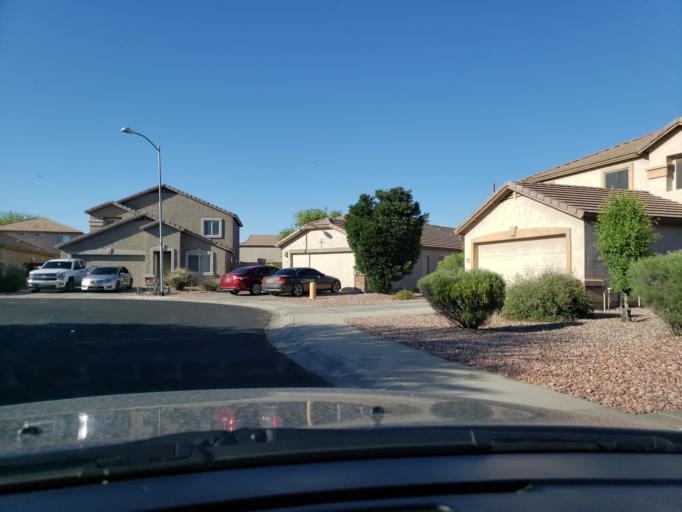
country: US
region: Arizona
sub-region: Maricopa County
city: Youngtown
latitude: 33.5720
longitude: -112.3077
